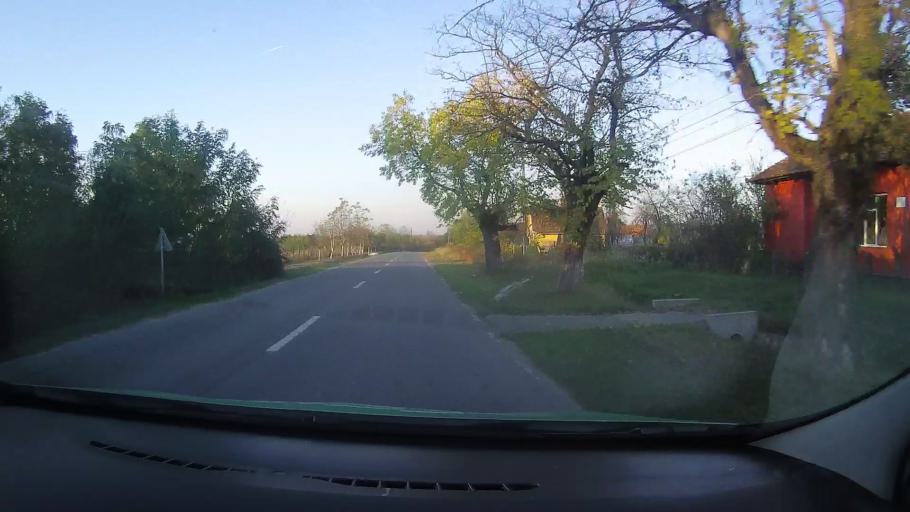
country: RO
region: Timis
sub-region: Comuna Traian Vuia
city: Traian Vuia
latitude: 45.7965
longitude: 22.0240
